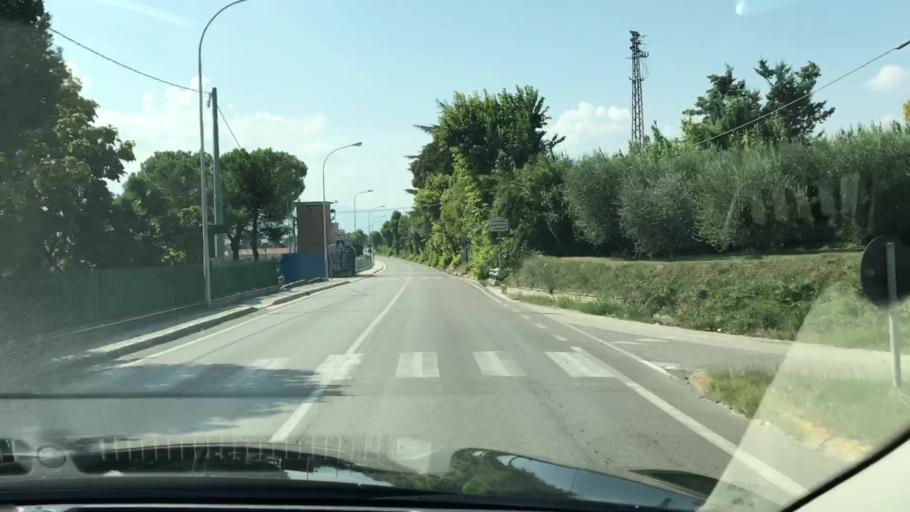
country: IT
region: The Marches
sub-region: Provincia di Ascoli Piceno
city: Stella
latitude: 42.8846
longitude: 13.8017
